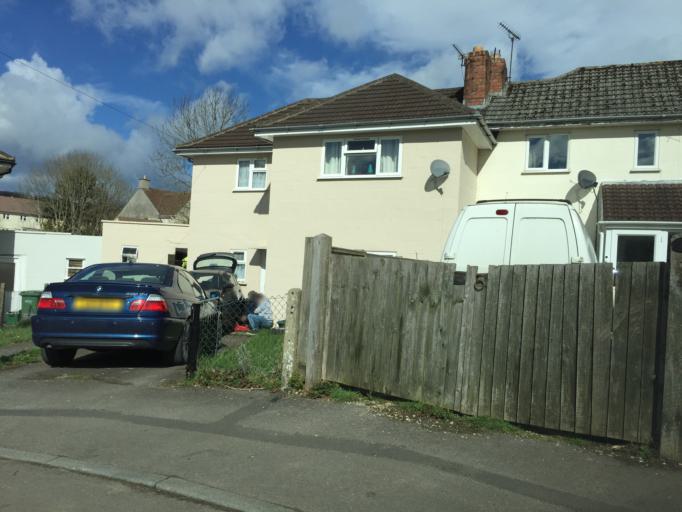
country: GB
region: England
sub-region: Gloucestershire
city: Wotton-under-Edge
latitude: 51.6354
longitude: -2.3438
